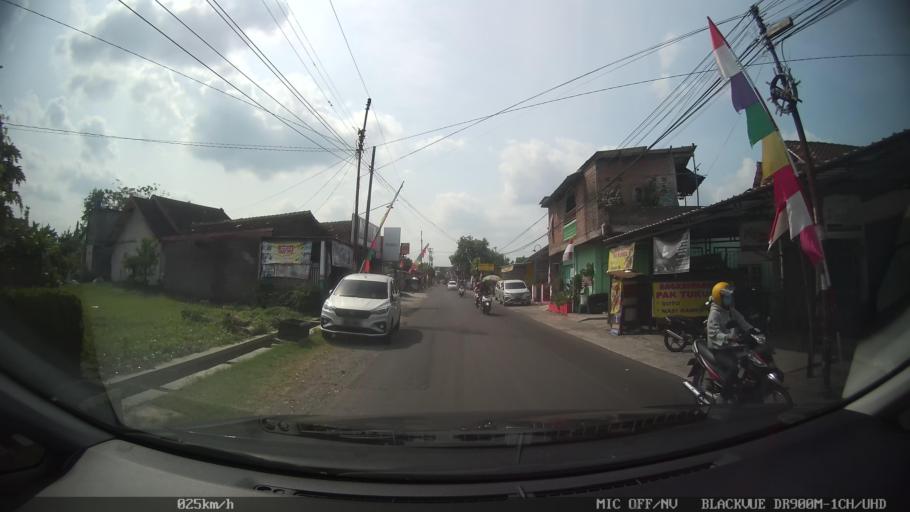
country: ID
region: Daerah Istimewa Yogyakarta
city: Depok
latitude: -7.7866
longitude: 110.4477
